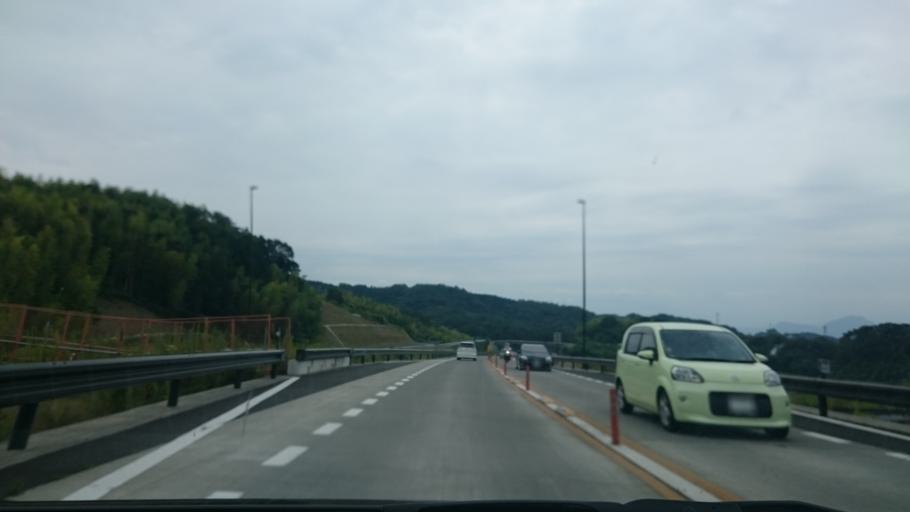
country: JP
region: Shizuoka
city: Mishima
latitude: 35.1219
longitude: 138.9489
